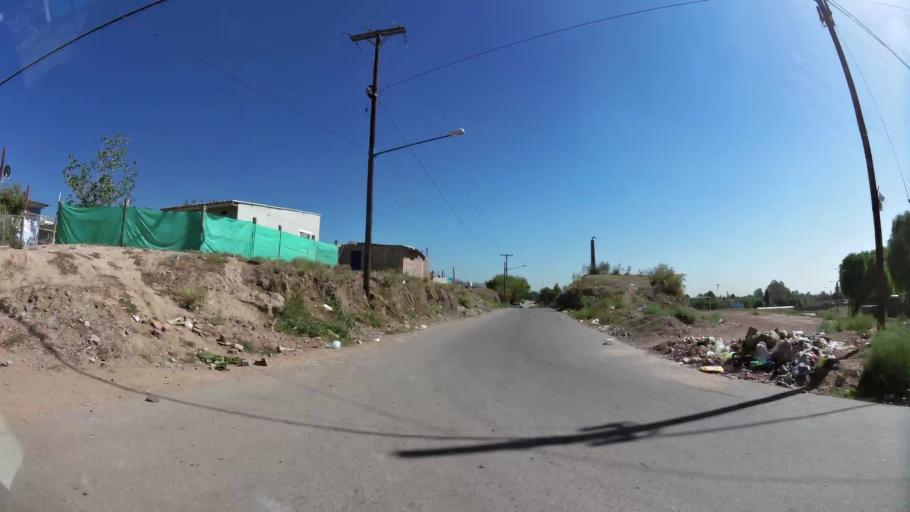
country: AR
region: Mendoza
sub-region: Departamento de Godoy Cruz
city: Godoy Cruz
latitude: -32.9130
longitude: -68.8821
